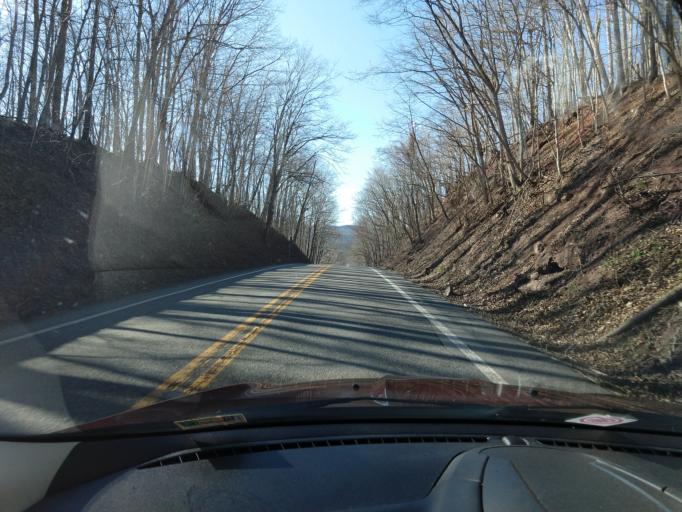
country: US
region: West Virginia
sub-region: Summers County
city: Hinton
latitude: 37.7393
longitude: -80.9135
